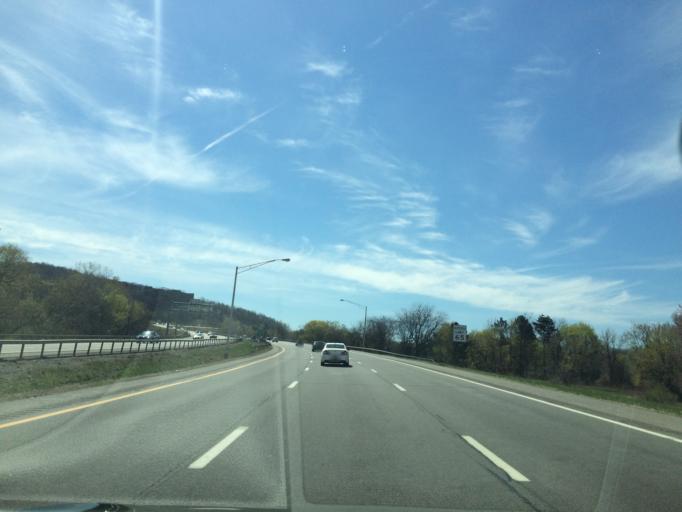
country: US
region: New York
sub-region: Monroe County
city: Fairport
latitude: 43.0539
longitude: -77.4704
